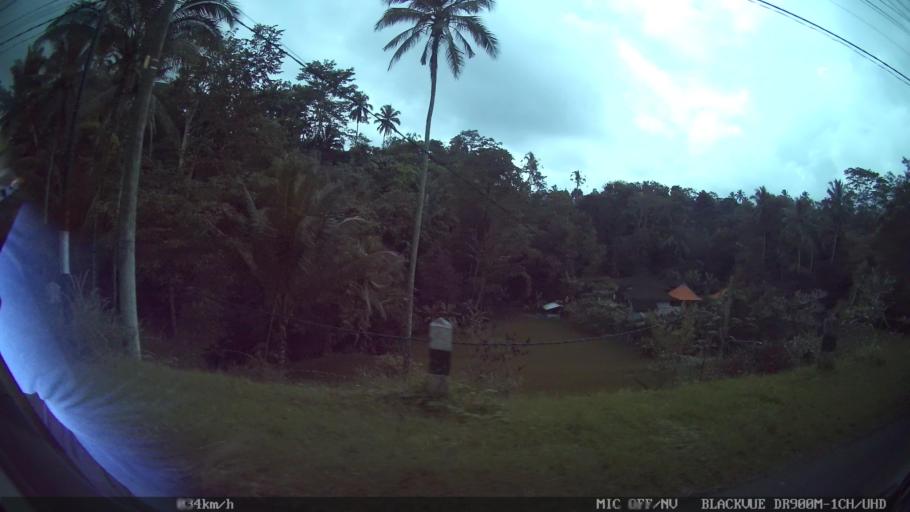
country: ID
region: Bali
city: Petang
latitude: -8.4053
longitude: 115.2217
